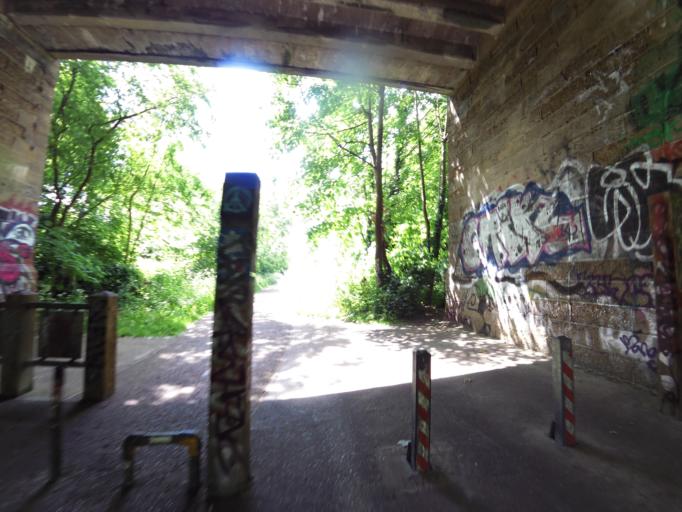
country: GB
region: England
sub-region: Norfolk
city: Norwich
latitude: 52.6427
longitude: 1.2757
